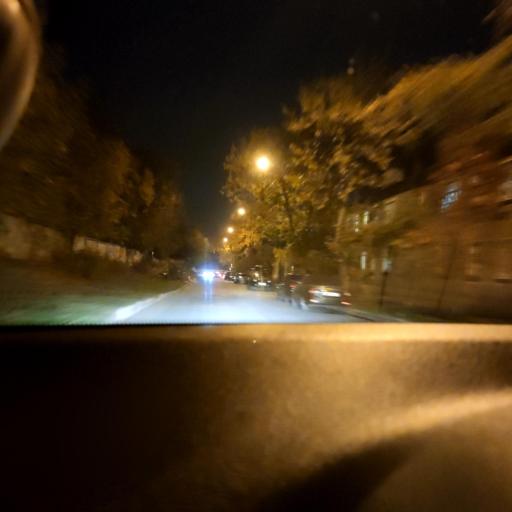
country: RU
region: Samara
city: Samara
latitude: 53.2200
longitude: 50.2358
